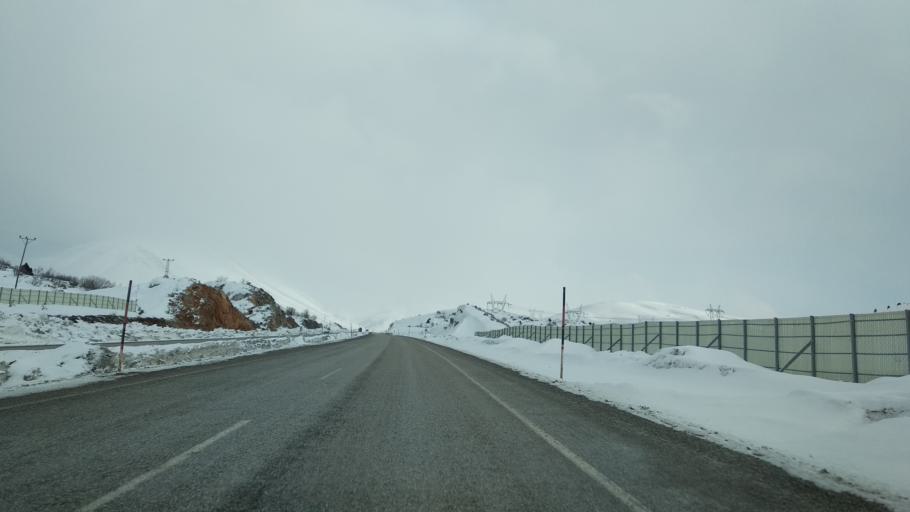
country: TR
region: Kahramanmaras
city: Goksun
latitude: 38.2069
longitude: 36.4326
